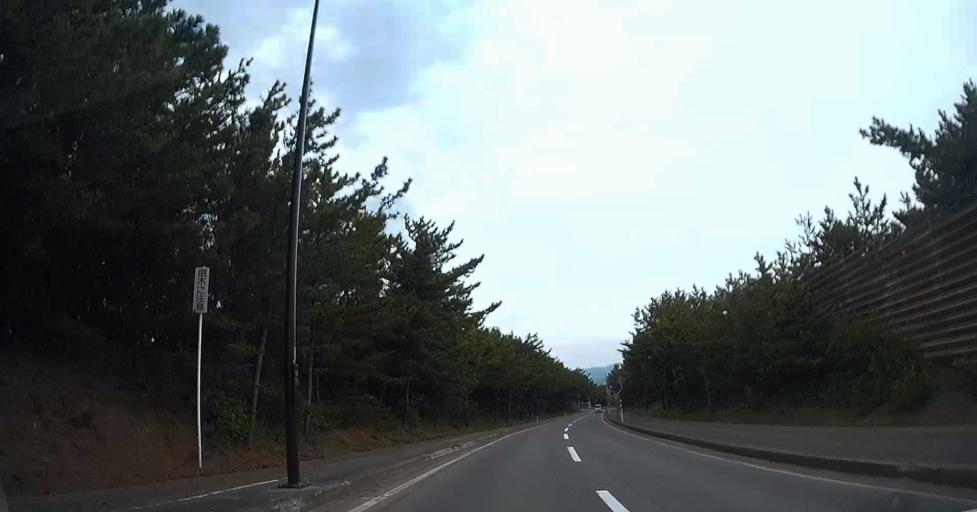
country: JP
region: Aomori
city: Shimokizukuri
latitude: 41.0411
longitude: 140.3255
